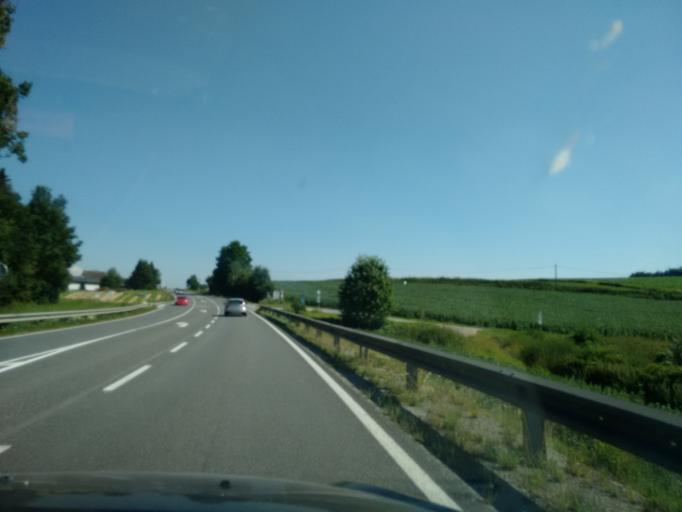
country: AT
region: Upper Austria
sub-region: Politischer Bezirk Grieskirchen
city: Bad Schallerbach
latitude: 48.2193
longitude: 13.9676
